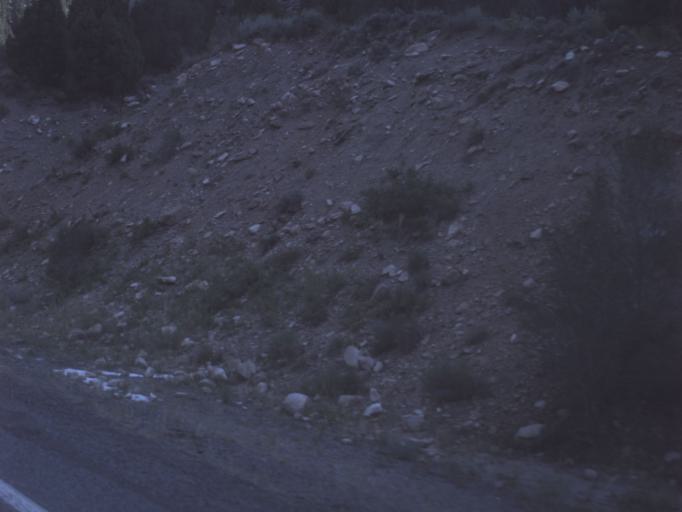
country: US
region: Utah
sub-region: Emery County
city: Huntington
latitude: 39.4627
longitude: -111.1447
